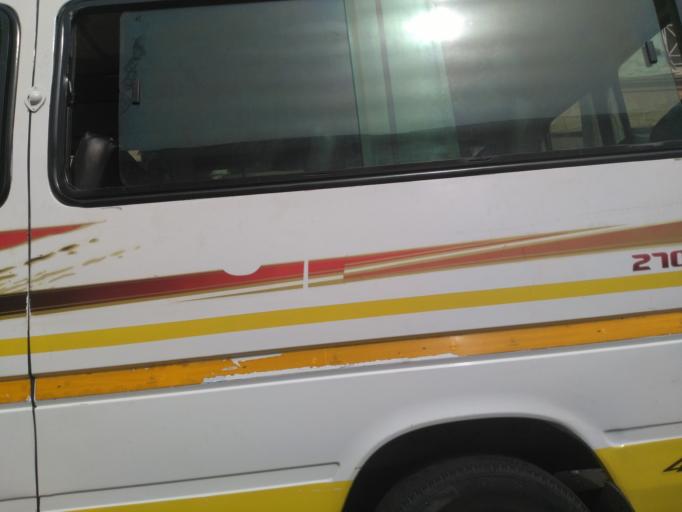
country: GH
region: Ashanti
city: Kumasi
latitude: 6.6949
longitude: -1.6201
